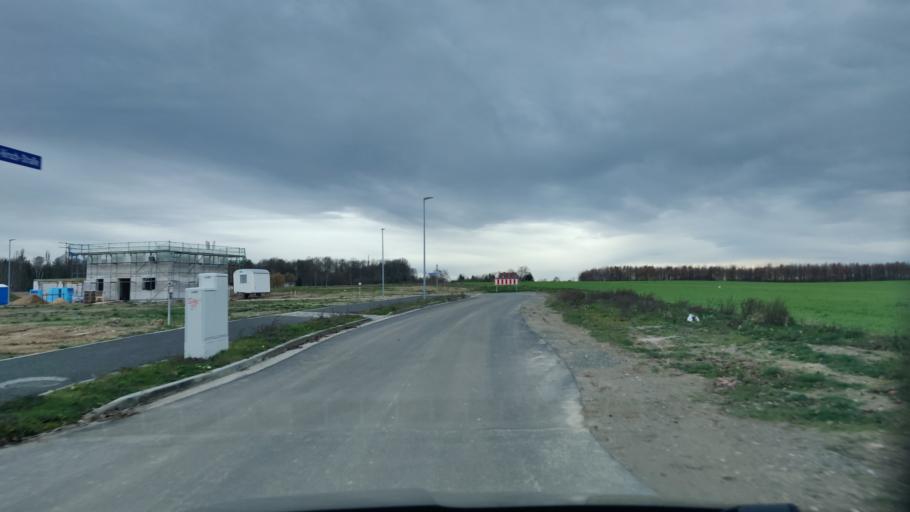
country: DE
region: Saxony
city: Bad Lausick
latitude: 51.1560
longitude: 12.6525
